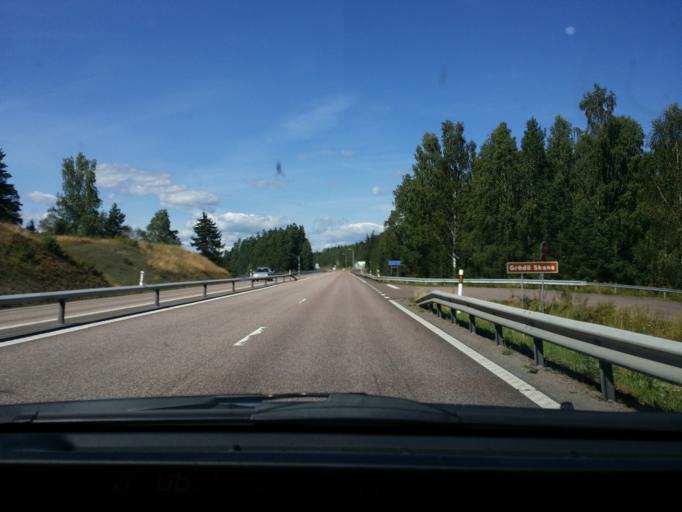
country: SE
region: Dalarna
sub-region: Hedemora Kommun
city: Brunna
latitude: 60.2382
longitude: 16.0300
